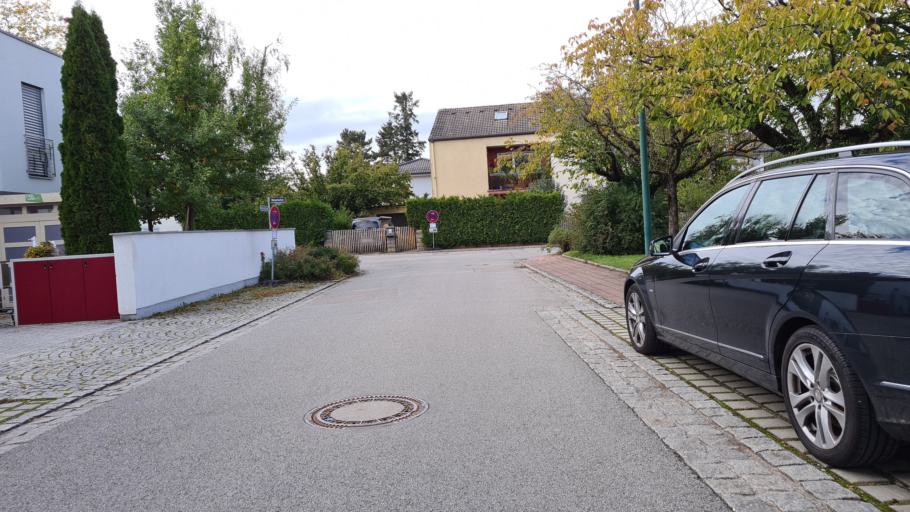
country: DE
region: Bavaria
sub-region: Upper Bavaria
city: Grafelfing
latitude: 48.1119
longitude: 11.4366
